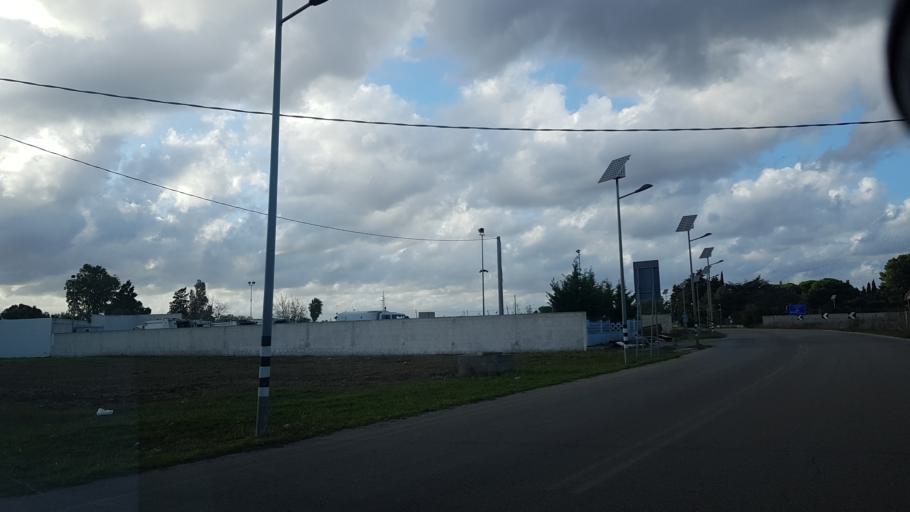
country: IT
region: Apulia
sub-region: Provincia di Brindisi
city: San Pietro Vernotico
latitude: 40.4980
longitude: 18.0059
